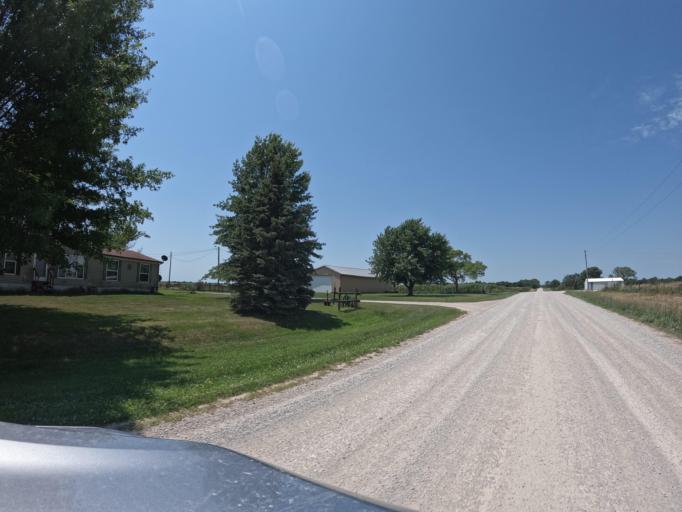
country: US
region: Iowa
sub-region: Appanoose County
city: Centerville
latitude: 40.7869
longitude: -92.9150
